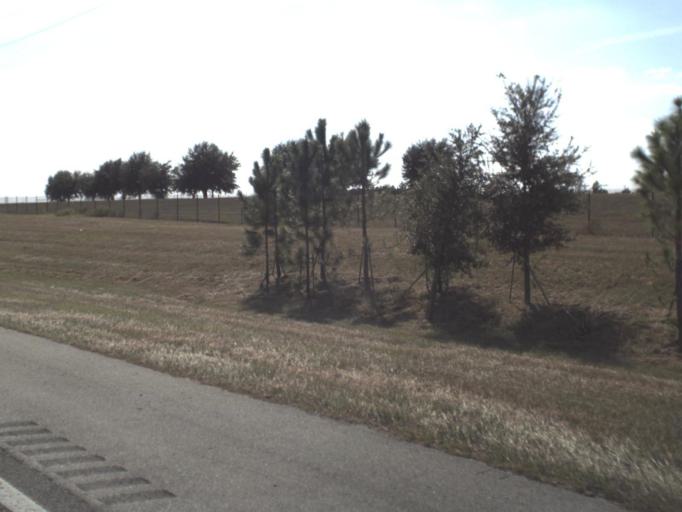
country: US
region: Florida
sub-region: Polk County
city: Citrus Ridge
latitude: 28.3986
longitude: -81.6219
